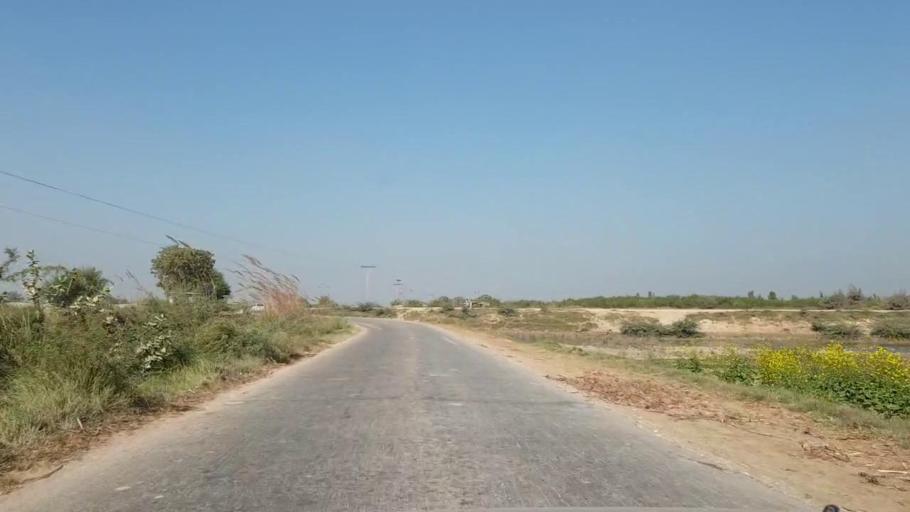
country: PK
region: Sindh
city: Tando Adam
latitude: 25.6489
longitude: 68.5907
